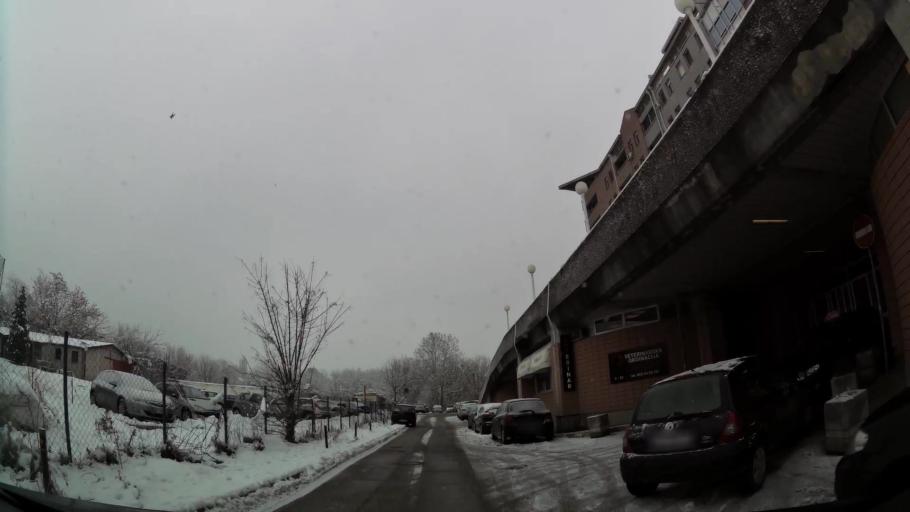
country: RS
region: Central Serbia
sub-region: Belgrade
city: Novi Beograd
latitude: 44.8232
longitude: 20.4213
